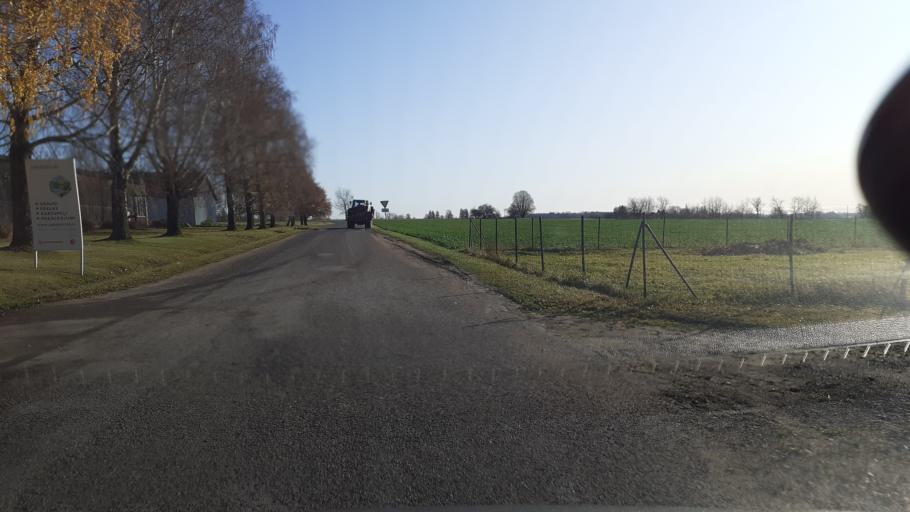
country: LV
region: Kuldigas Rajons
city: Kuldiga
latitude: 56.9970
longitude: 21.8983
